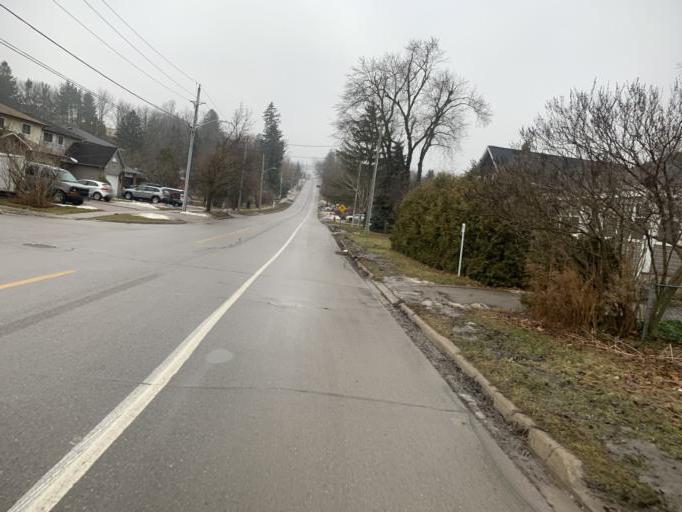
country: CA
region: Ontario
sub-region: Halton
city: Milton
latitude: 43.6599
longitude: -79.9176
